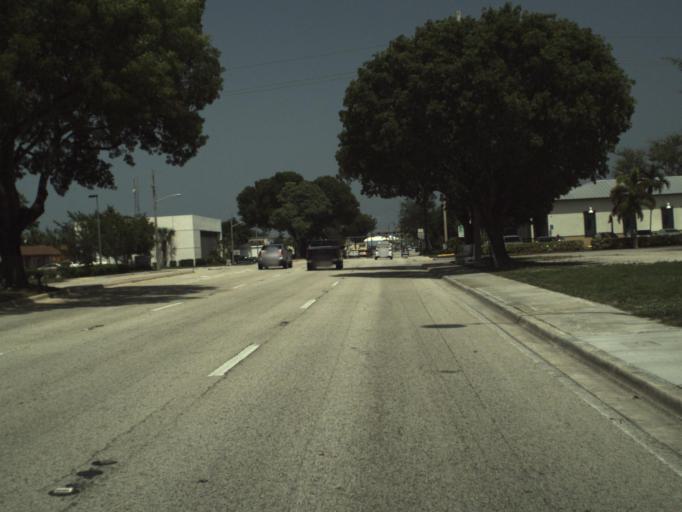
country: US
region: Florida
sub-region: Broward County
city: Deerfield Beach
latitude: 26.3186
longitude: -80.1046
